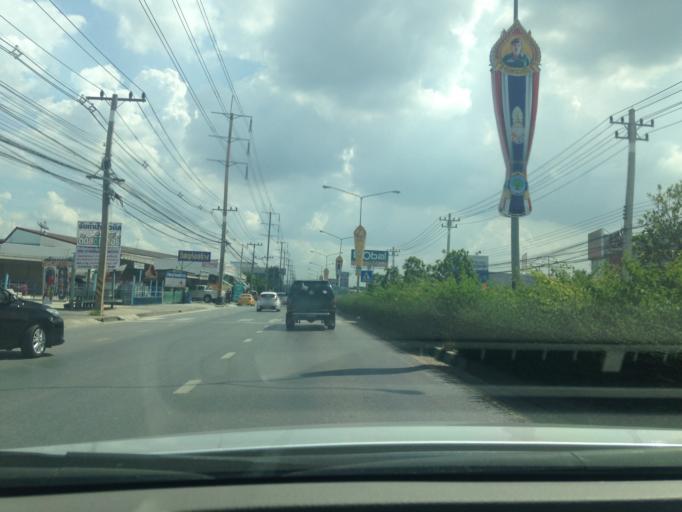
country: TH
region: Pathum Thani
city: Pathum Thani
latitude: 14.0391
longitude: 100.5251
